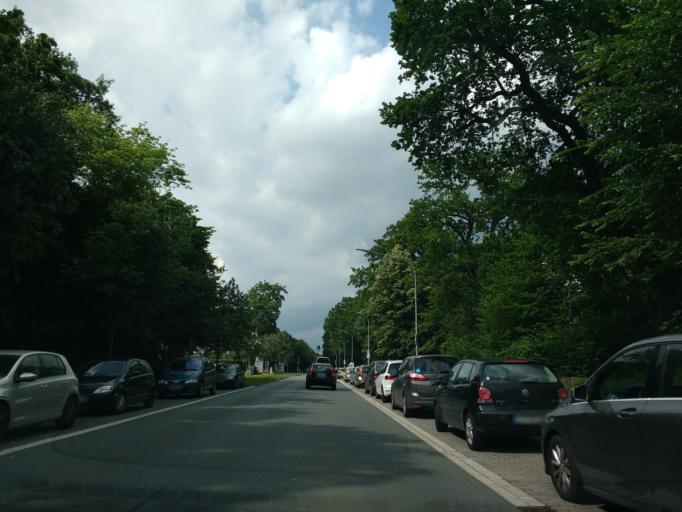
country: DE
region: North Rhine-Westphalia
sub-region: Regierungsbezirk Detmold
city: Lemgo
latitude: 52.0364
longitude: 8.9026
